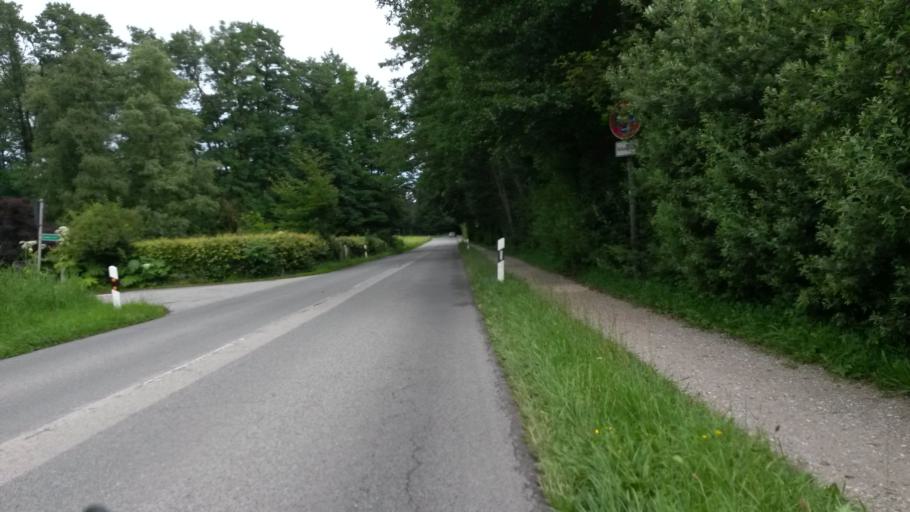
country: DE
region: Bavaria
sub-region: Upper Bavaria
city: Prien am Chiemsee
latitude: 47.8421
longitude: 12.3709
